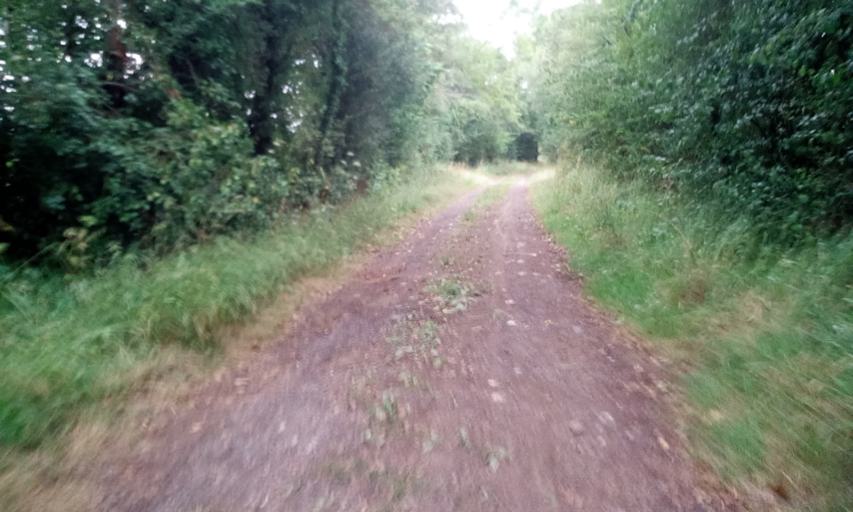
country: FR
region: Lower Normandy
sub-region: Departement du Calvados
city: Sannerville
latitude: 49.1884
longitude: -0.2172
